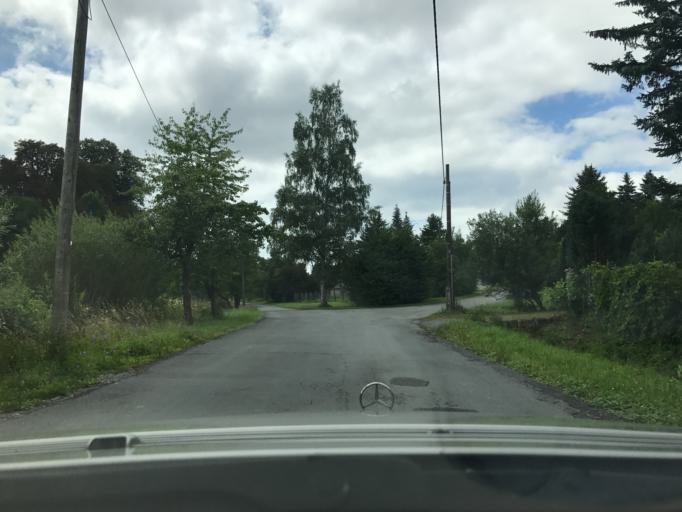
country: DE
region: Thuringia
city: Muehlhausen
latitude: 51.2083
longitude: 10.4309
